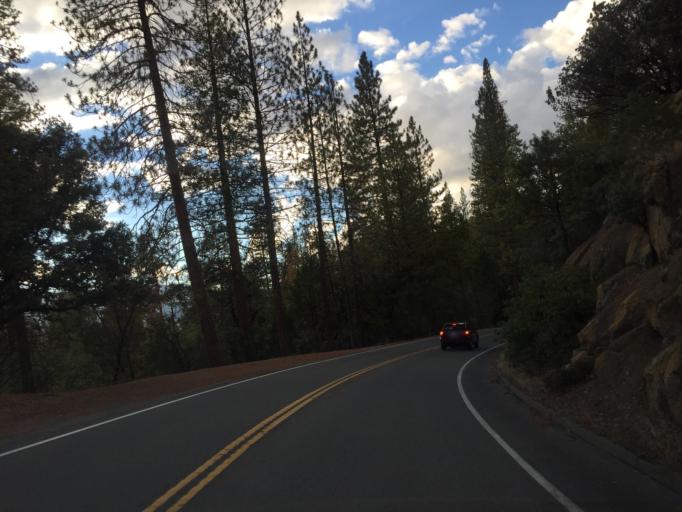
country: US
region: California
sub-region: Madera County
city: Ahwahnee
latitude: 37.5287
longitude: -119.6322
